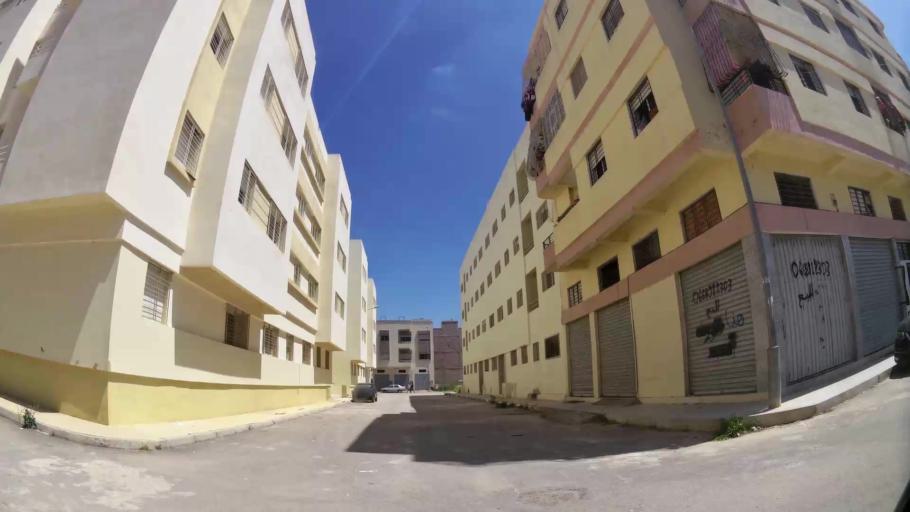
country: MA
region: Fes-Boulemane
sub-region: Fes
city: Fes
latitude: 34.0235
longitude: -5.0483
